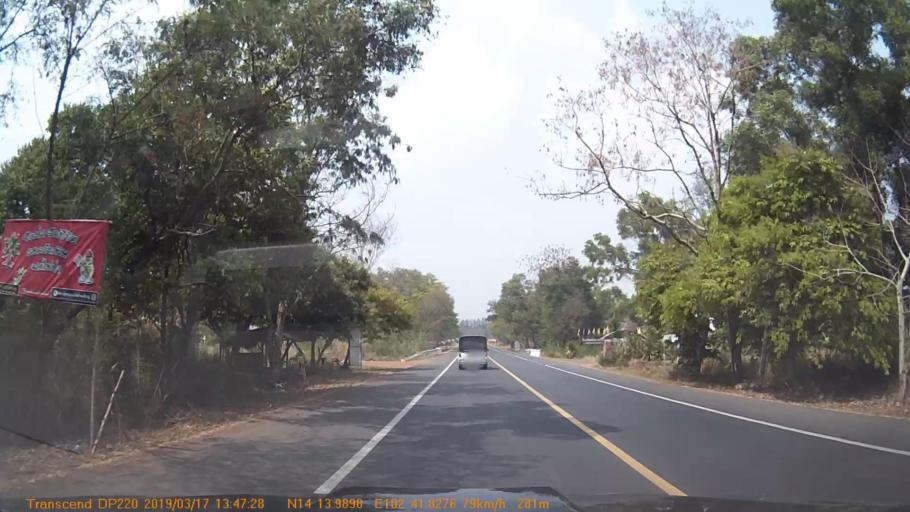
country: TH
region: Buriram
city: Non Din Daeng
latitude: 14.2335
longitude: 102.6971
